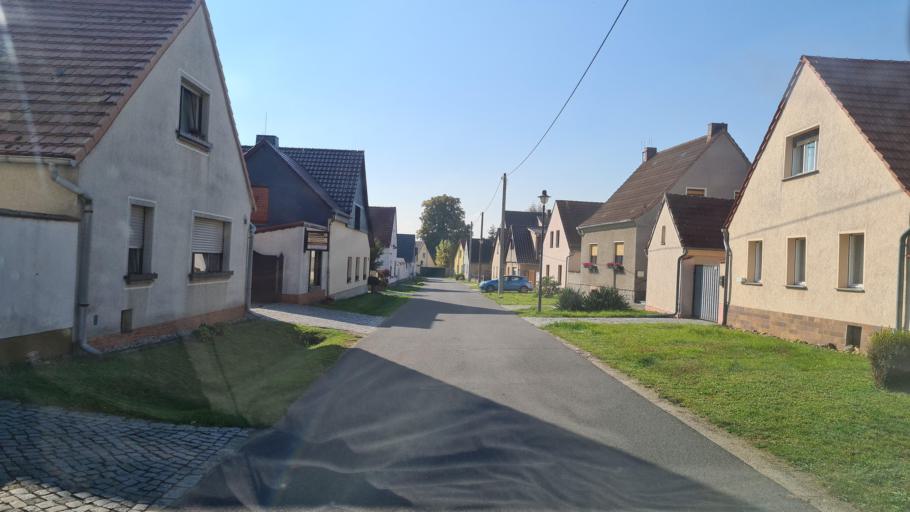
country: DE
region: Brandenburg
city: Luckau
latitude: 51.8474
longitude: 13.7039
